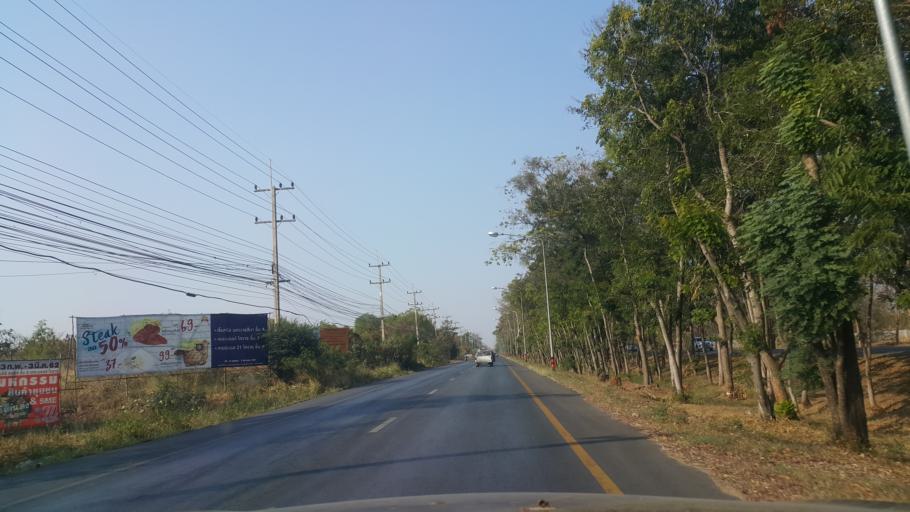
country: TH
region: Nakhon Ratchasima
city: Nakhon Ratchasima
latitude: 14.8828
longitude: 102.0714
